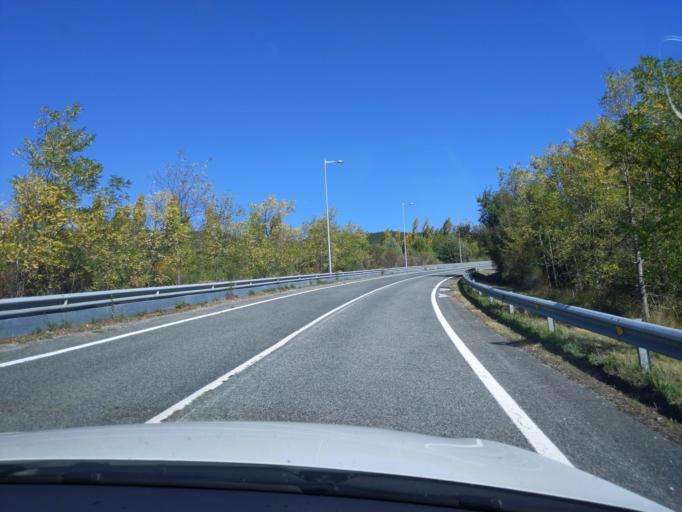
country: ES
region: Navarre
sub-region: Provincia de Navarra
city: Egues-Uharte
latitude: 42.8316
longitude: -1.5720
